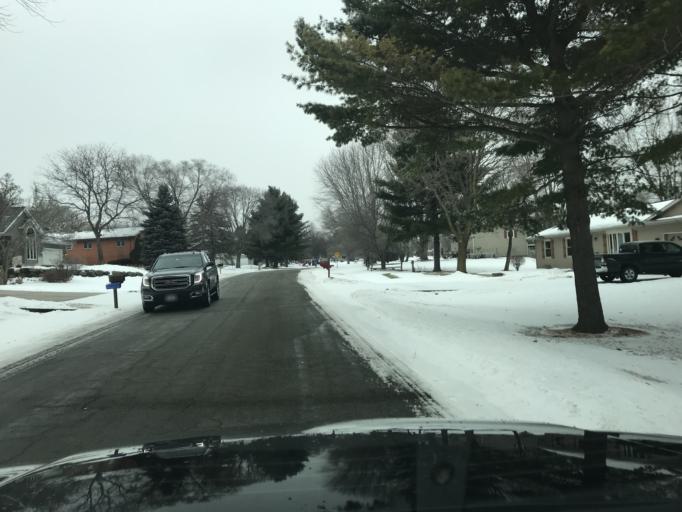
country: US
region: Wisconsin
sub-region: Dane County
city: Cottage Grove
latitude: 43.0982
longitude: -89.2164
